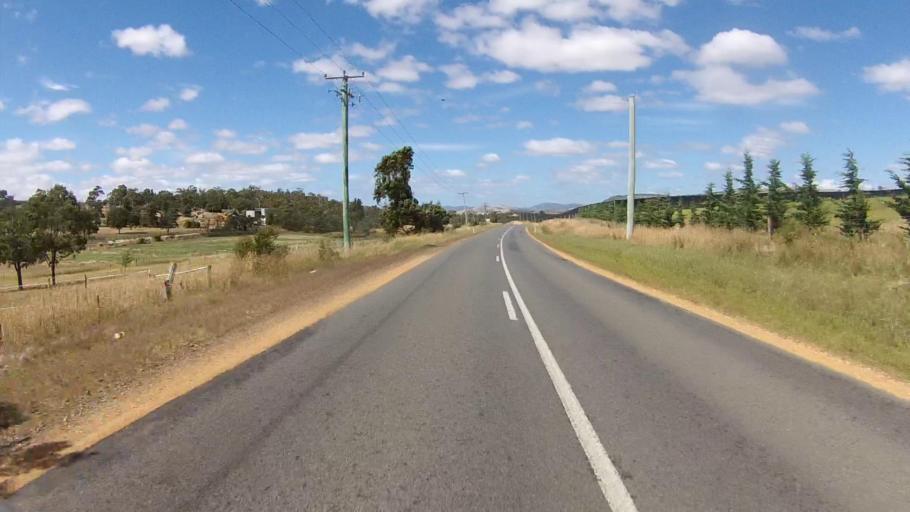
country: AU
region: Tasmania
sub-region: Sorell
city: Sorell
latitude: -42.6447
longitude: 147.4340
